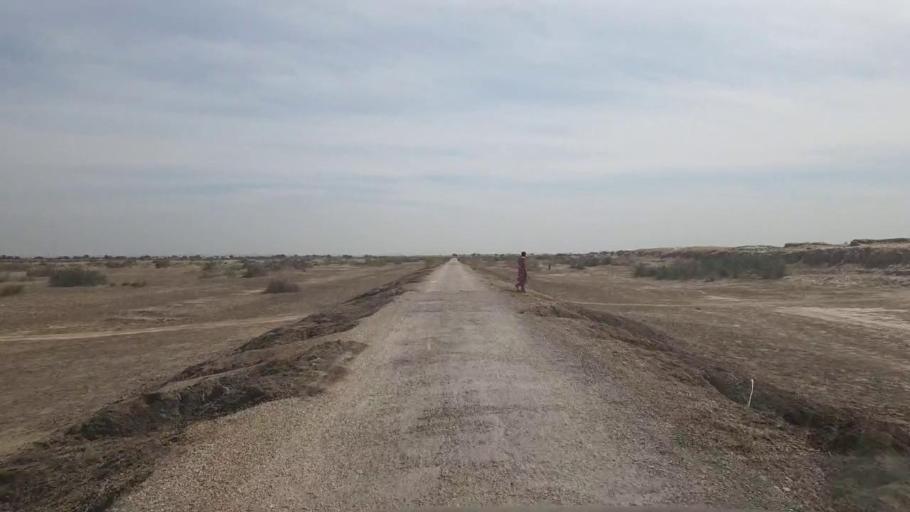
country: PK
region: Sindh
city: Kunri
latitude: 25.2192
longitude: 69.6204
